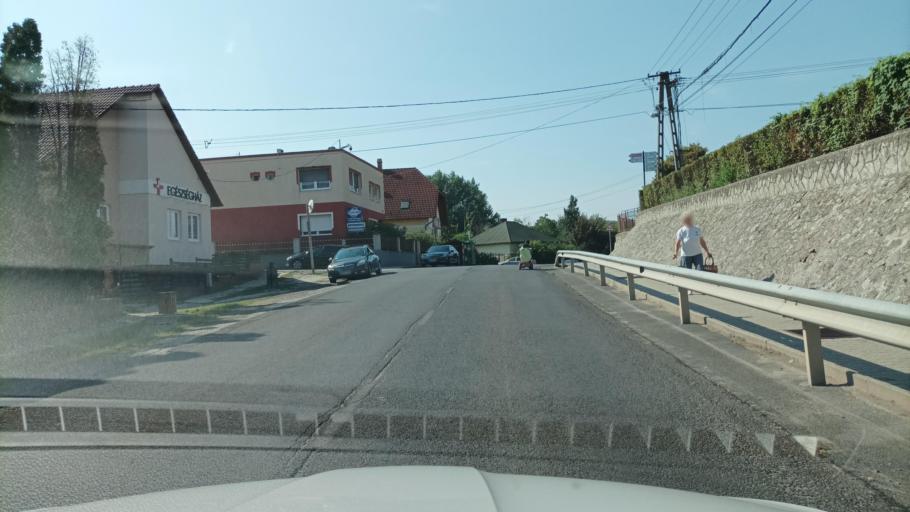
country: HU
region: Pest
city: Valko
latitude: 47.5674
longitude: 19.5116
